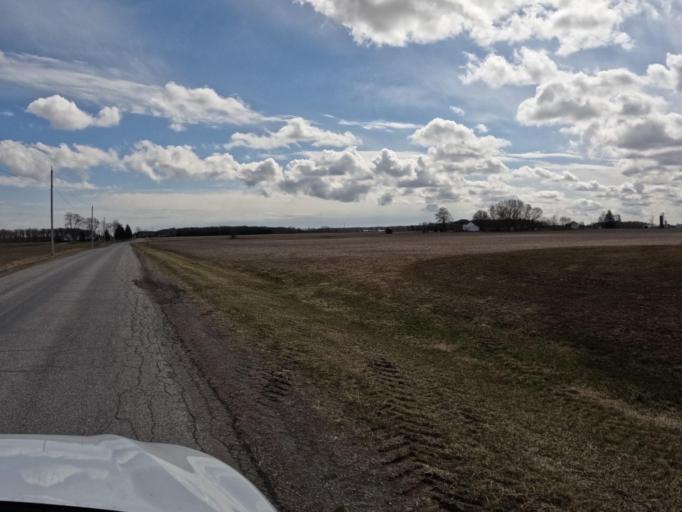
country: CA
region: Ontario
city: Norfolk County
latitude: 42.9167
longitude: -80.1959
